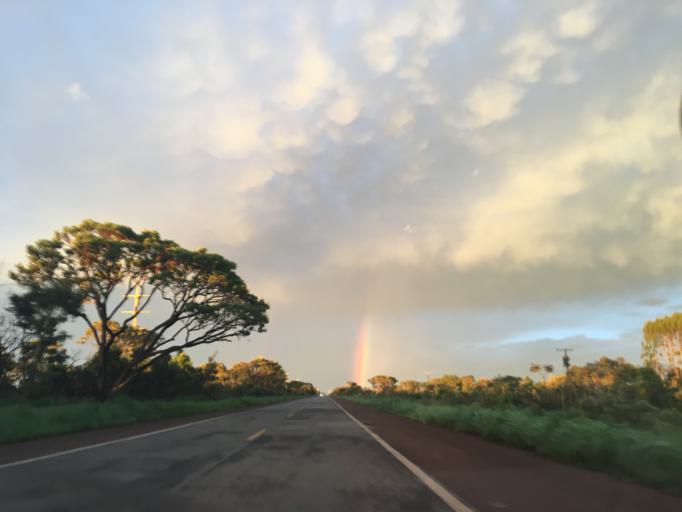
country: BR
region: Federal District
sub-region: Brasilia
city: Brasilia
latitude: -15.9787
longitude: -47.9180
